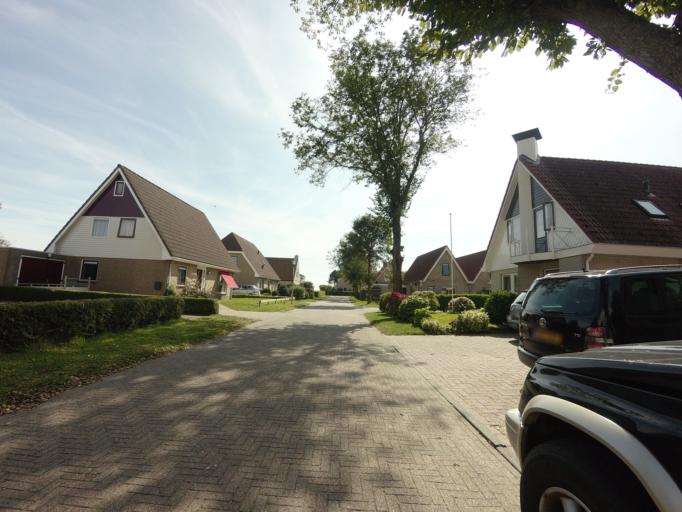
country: NL
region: Friesland
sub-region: Gemeente Ameland
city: Hollum
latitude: 53.4433
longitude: 5.6898
